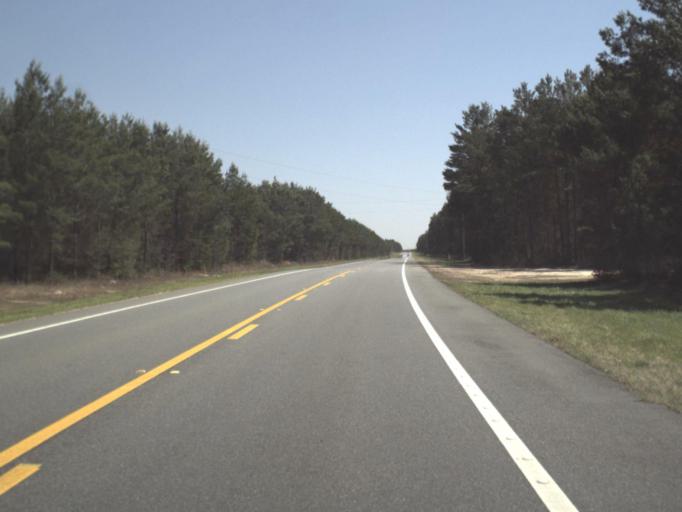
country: US
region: Florida
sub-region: Bay County
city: Youngstown
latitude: 30.4352
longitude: -85.3357
